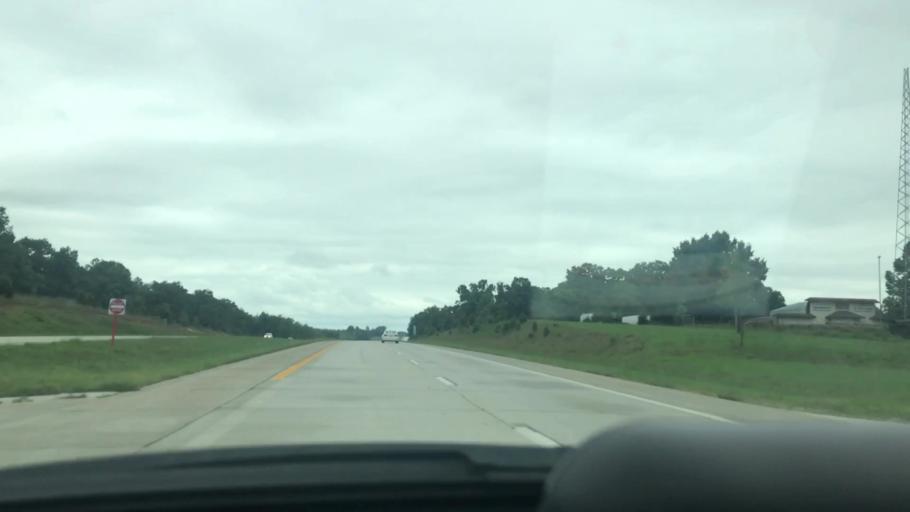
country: US
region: Missouri
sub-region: Dallas County
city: Buffalo
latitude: 37.5397
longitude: -93.1376
